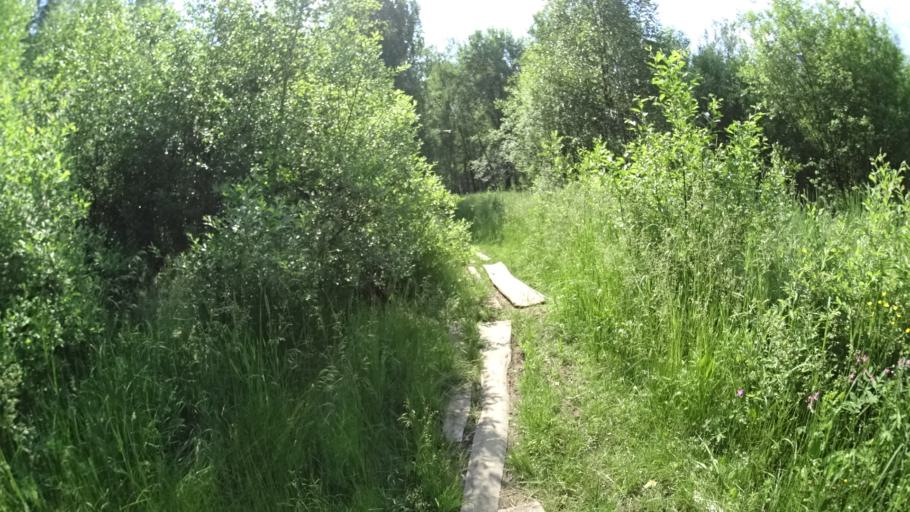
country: RU
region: Moskovskaya
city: Lesnoy
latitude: 56.0810
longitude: 37.9408
